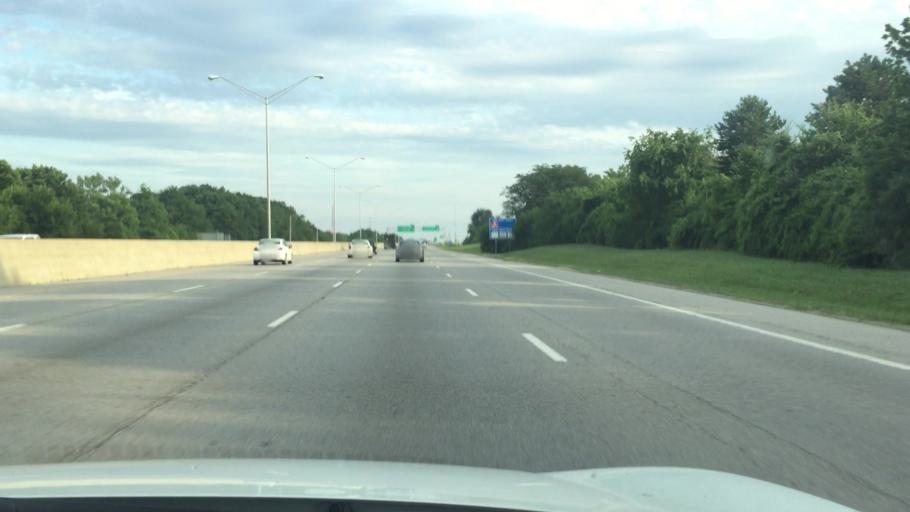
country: US
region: Ohio
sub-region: Franklin County
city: Grandview Heights
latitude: 40.0126
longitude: -83.0324
